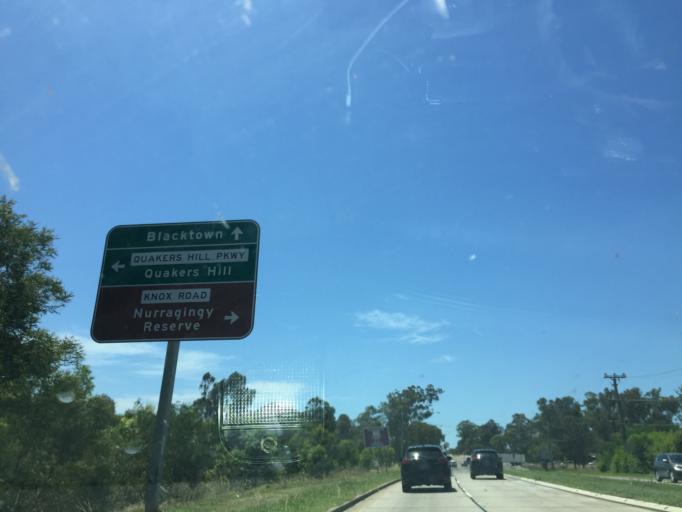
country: AU
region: New South Wales
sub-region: Blacktown
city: Glendenning
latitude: -33.7418
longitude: 150.8679
